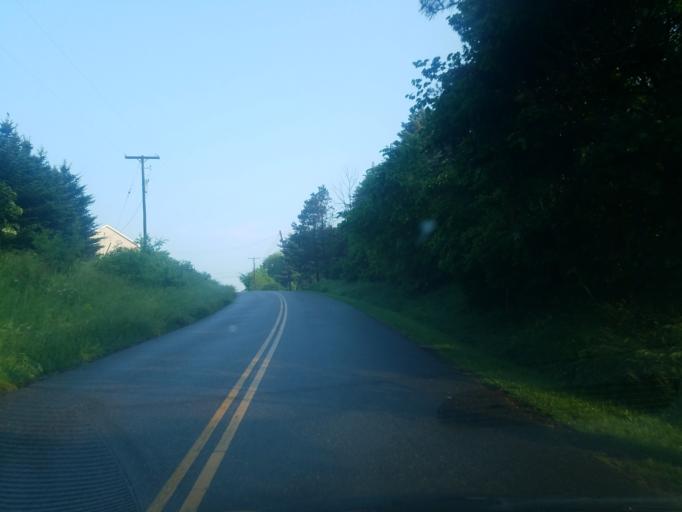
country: US
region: Ohio
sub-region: Stark County
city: Minerva
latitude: 40.7162
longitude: -81.0927
